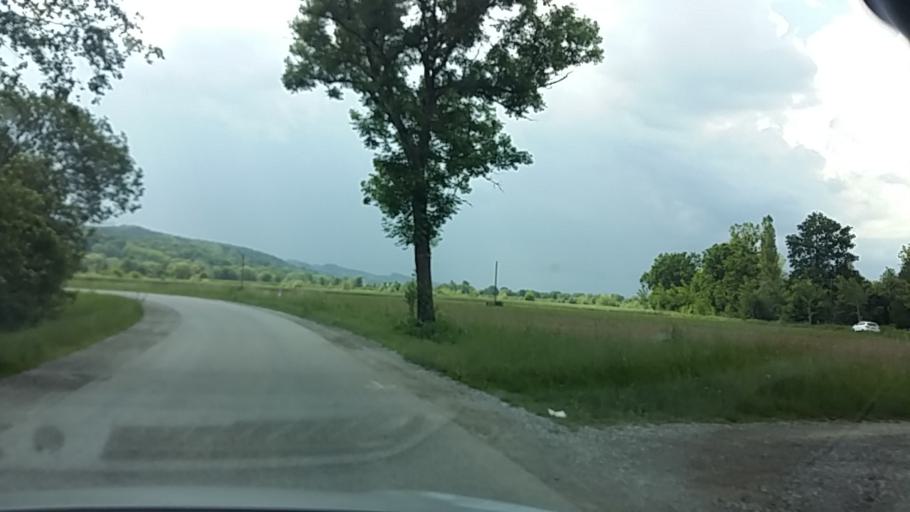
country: AT
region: Styria
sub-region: Politischer Bezirk Hartberg-Fuerstenfeld
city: Soechau
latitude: 47.0656
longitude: 16.0135
